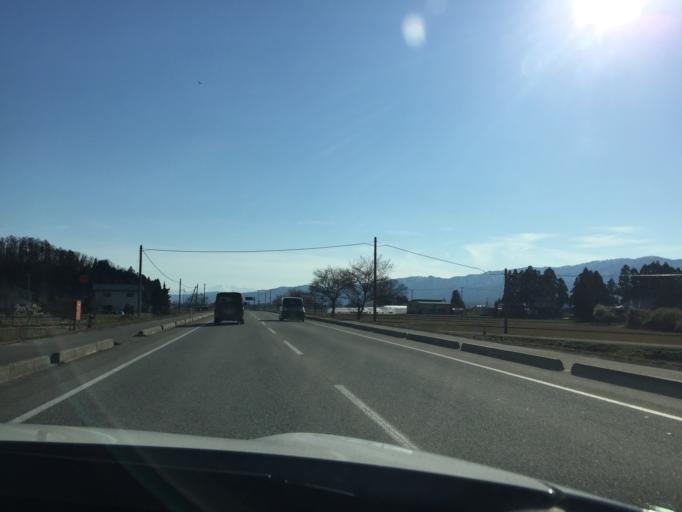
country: JP
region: Yamagata
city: Nagai
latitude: 38.1561
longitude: 140.0700
